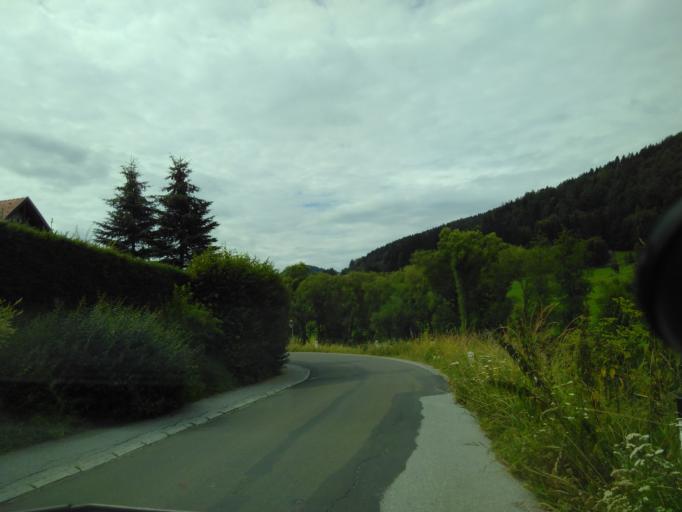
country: AT
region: Styria
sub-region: Politischer Bezirk Graz-Umgebung
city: Semriach
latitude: 47.2224
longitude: 15.3932
